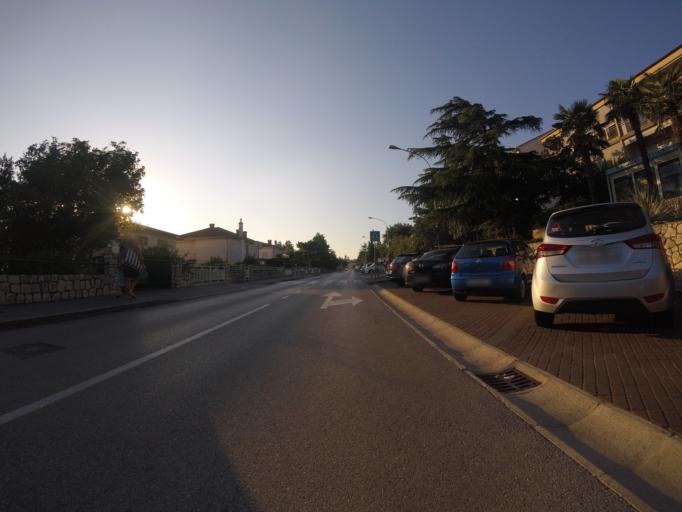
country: HR
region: Primorsko-Goranska
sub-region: Grad Crikvenica
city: Crikvenica
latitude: 45.1833
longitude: 14.6812
